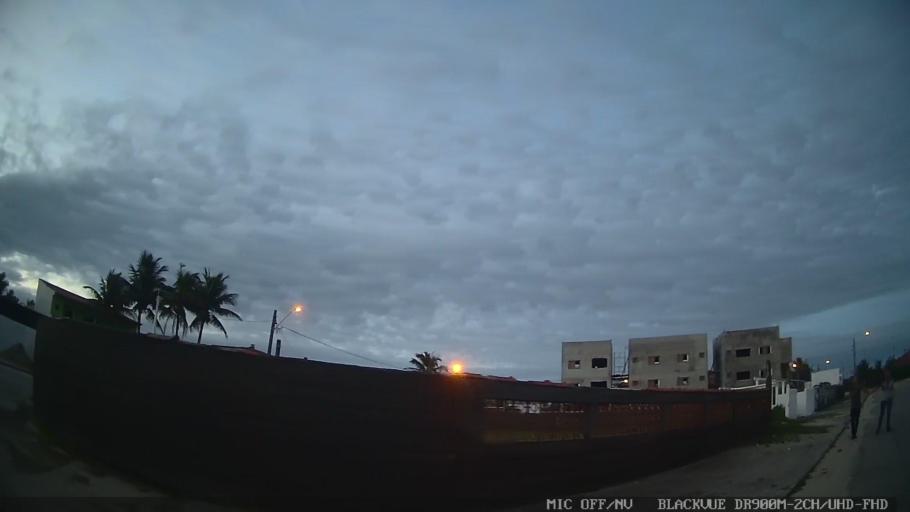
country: BR
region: Sao Paulo
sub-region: Itanhaem
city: Itanhaem
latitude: -24.2477
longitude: -46.8921
